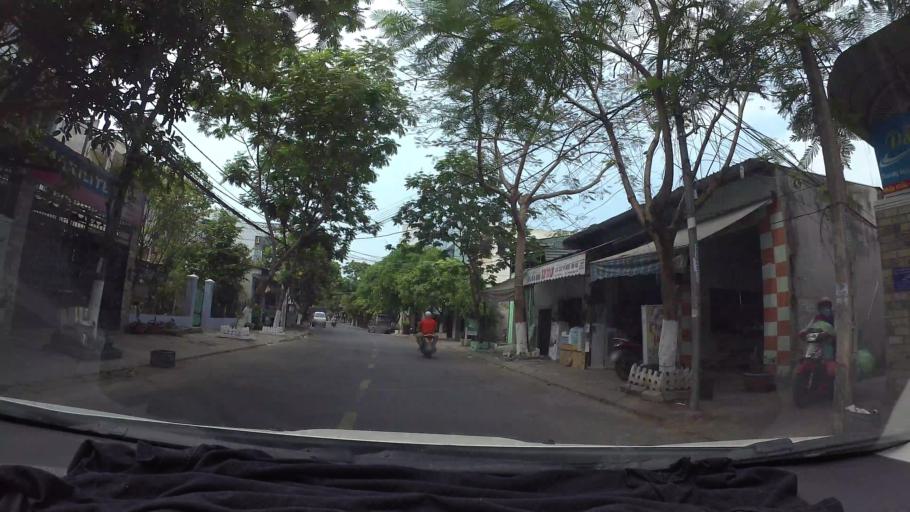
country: VN
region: Da Nang
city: Thanh Khe
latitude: 16.0516
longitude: 108.1800
